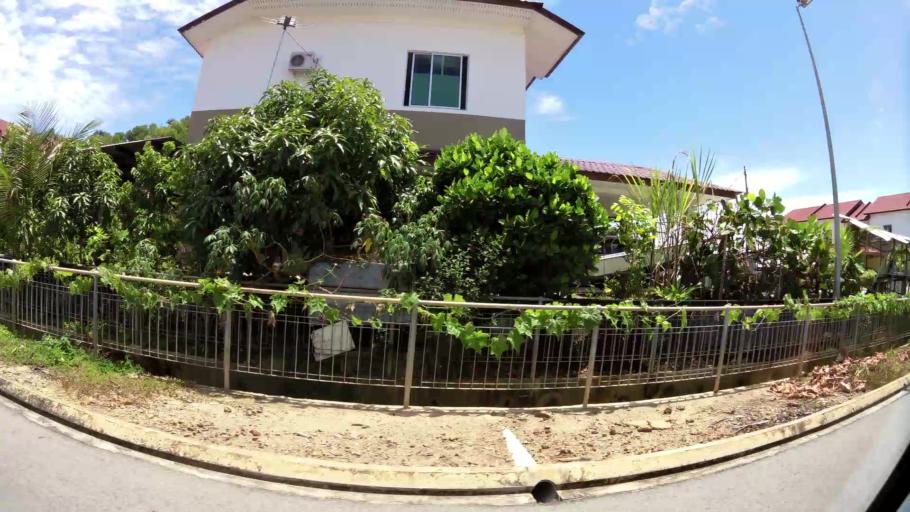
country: BN
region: Brunei and Muara
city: Bandar Seri Begawan
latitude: 5.0111
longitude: 115.0223
